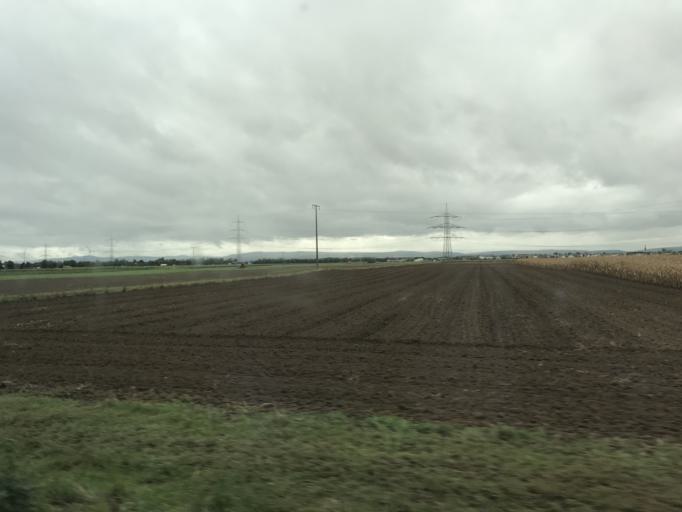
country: DE
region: Rheinland-Pfalz
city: Frankenthal
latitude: 49.5591
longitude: 8.3500
